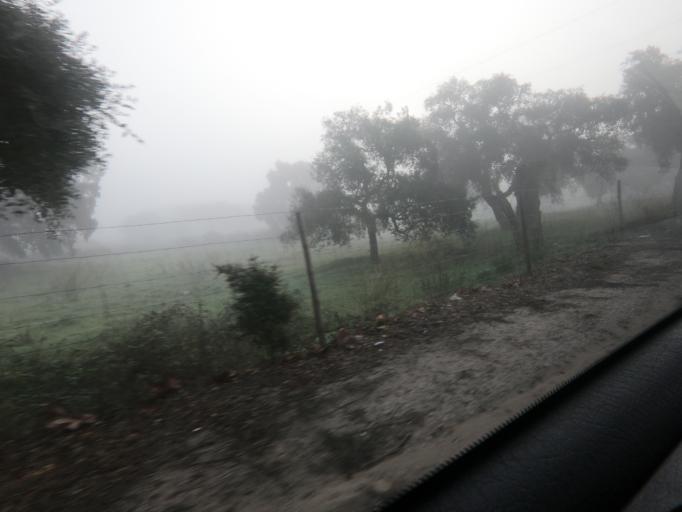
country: PT
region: Setubal
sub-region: Palmela
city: Palmela
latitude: 38.5759
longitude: -8.8327
